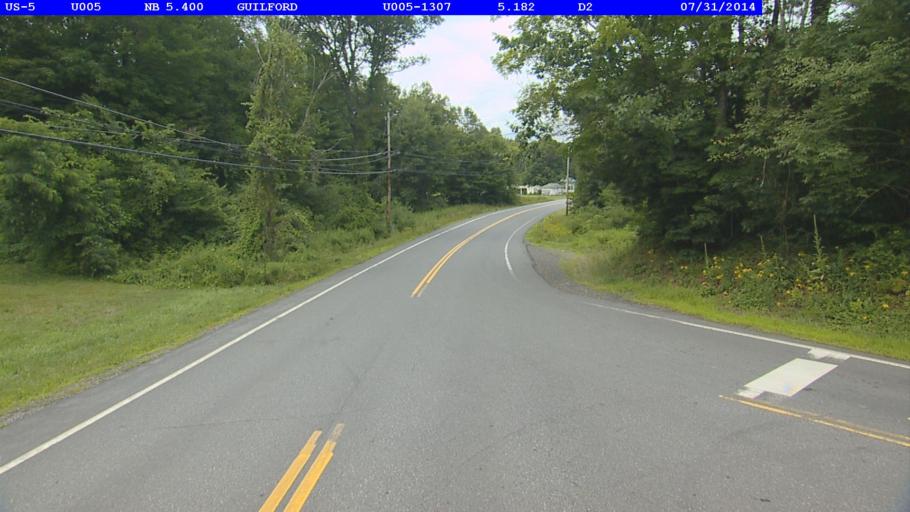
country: US
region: Vermont
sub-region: Windham County
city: Brattleboro
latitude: 42.8047
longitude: -72.5657
